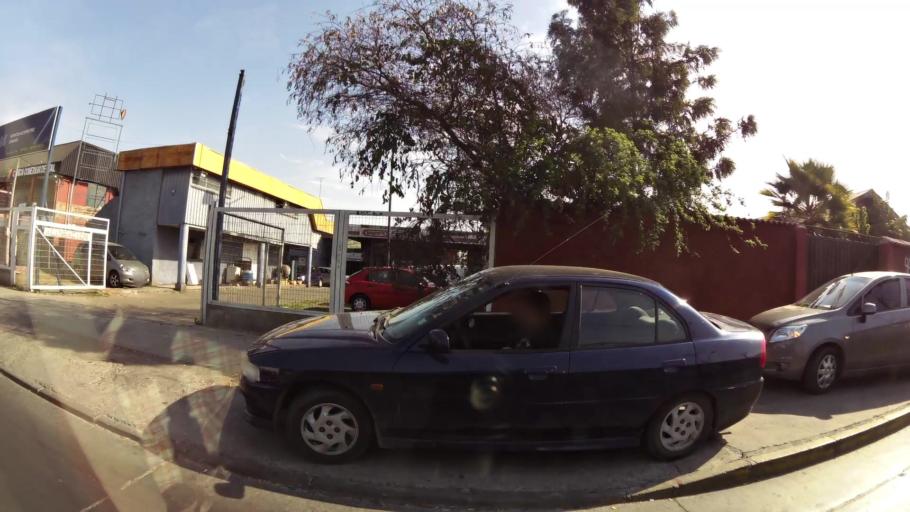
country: CL
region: Santiago Metropolitan
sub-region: Provincia de Cordillera
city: Puente Alto
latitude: -33.5636
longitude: -70.5840
